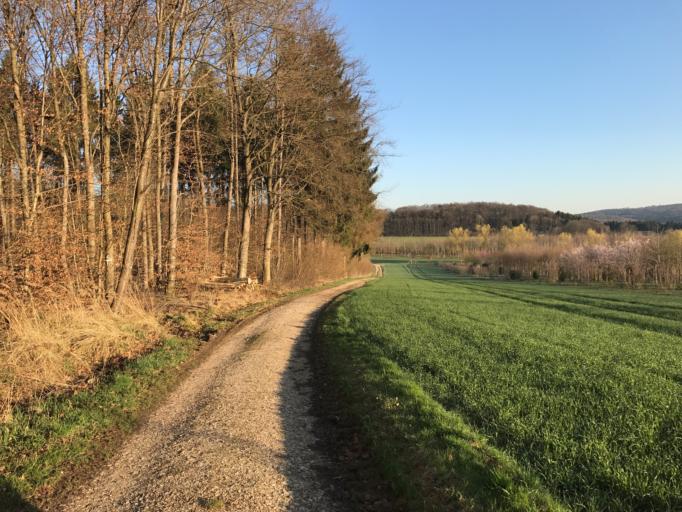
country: DE
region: Baden-Wuerttemberg
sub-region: Regierungsbezirk Stuttgart
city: Hochdorf
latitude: 48.6895
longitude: 9.4480
